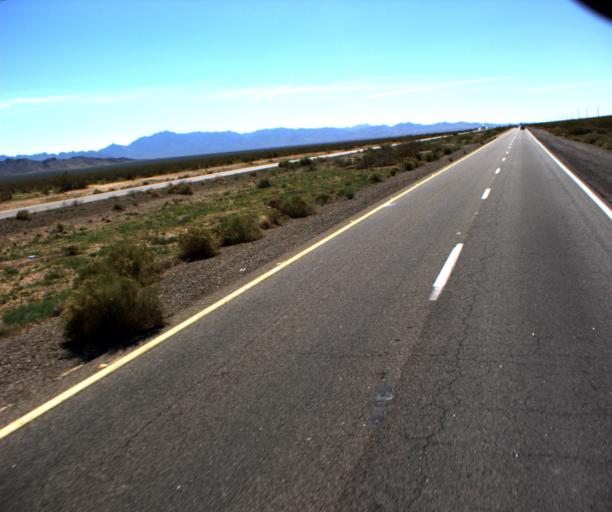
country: US
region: Arizona
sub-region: Mohave County
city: Dolan Springs
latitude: 35.6372
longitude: -114.4320
